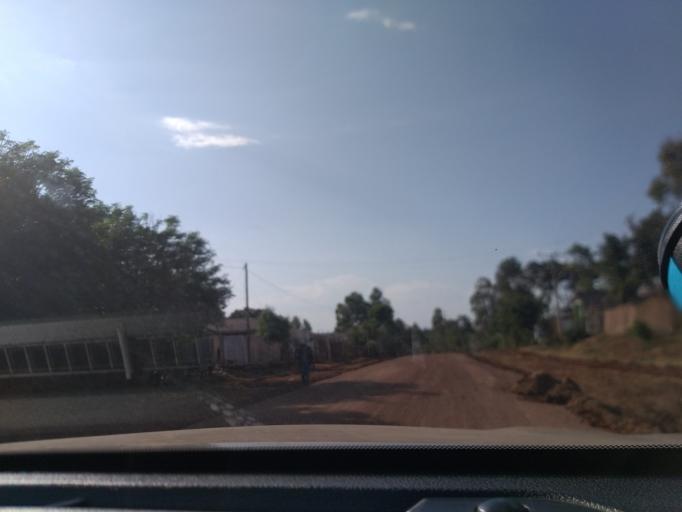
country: ET
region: Oromiya
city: Shashemene
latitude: 7.4269
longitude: 38.8115
